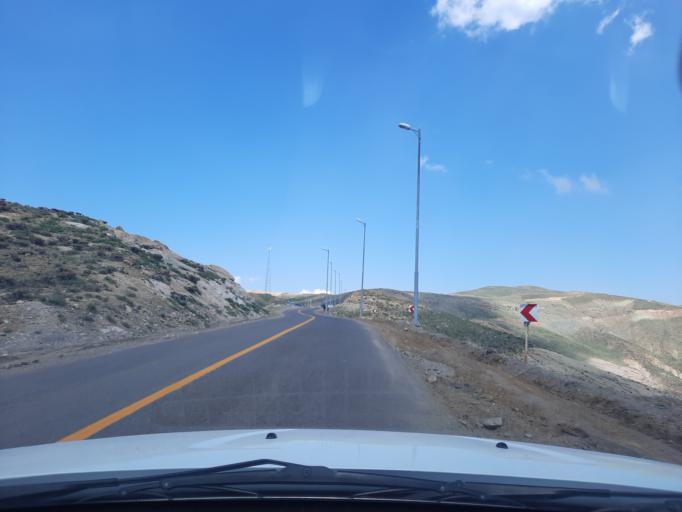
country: IR
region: Qazvin
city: Qazvin
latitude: 36.3813
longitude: 50.2026
